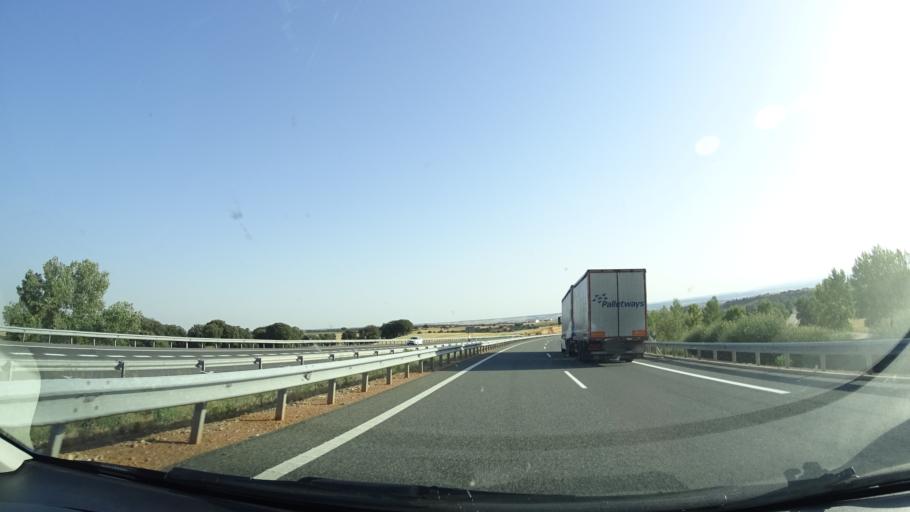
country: ES
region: Castille and Leon
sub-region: Provincia de Burgos
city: Quintanilla de la Mata
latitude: 41.9761
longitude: -3.7768
